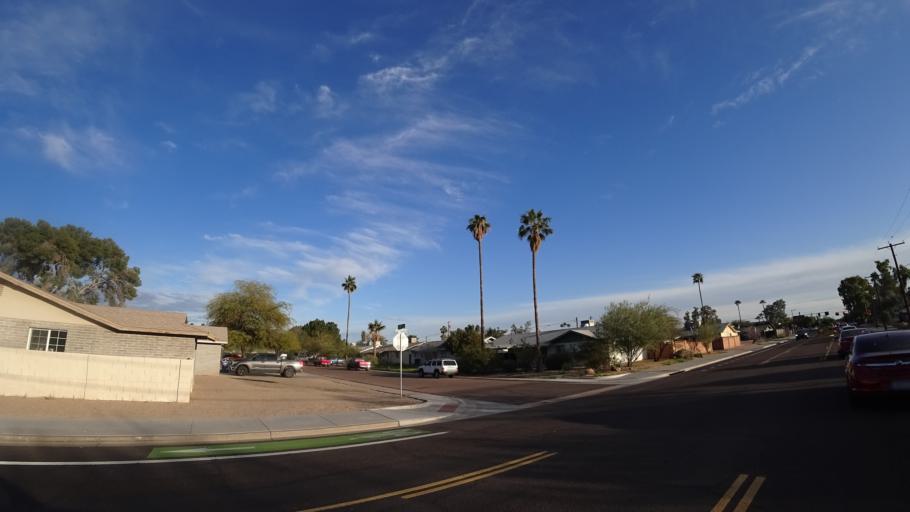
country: US
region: Arizona
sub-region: Maricopa County
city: Tempe Junction
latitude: 33.4092
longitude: -111.9522
